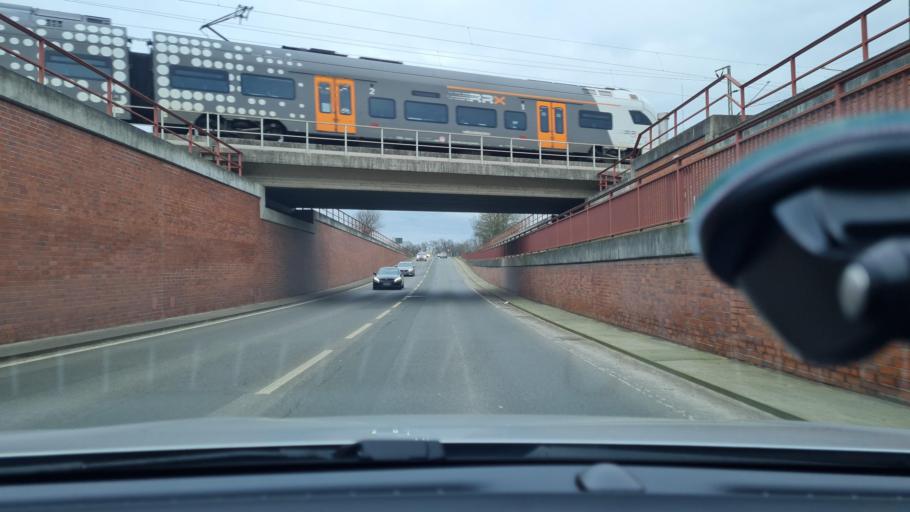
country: DE
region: North Rhine-Westphalia
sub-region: Regierungsbezirk Dusseldorf
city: Voerde
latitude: 51.6069
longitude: 6.6732
